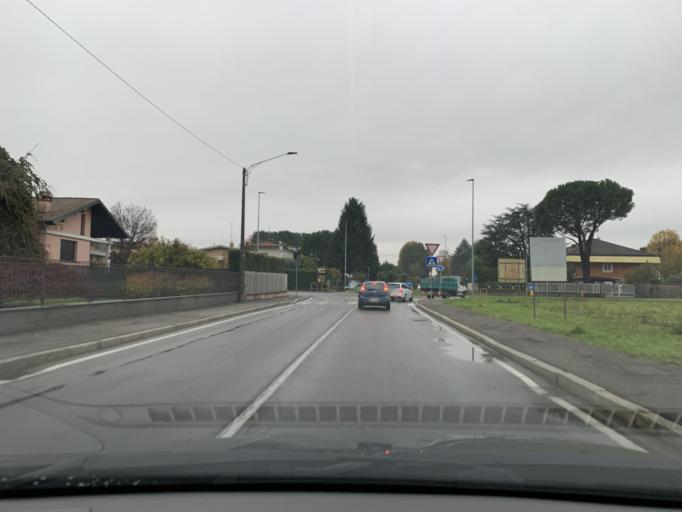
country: IT
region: Lombardy
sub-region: Provincia di Como
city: Rovellasca
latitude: 45.6612
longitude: 9.0535
